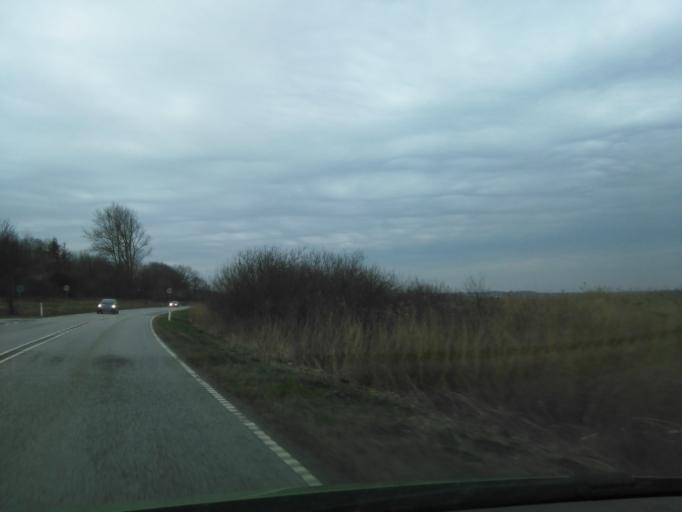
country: DK
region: North Denmark
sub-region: Mariagerfjord Kommune
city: Hadsund
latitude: 56.6949
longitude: 10.1111
